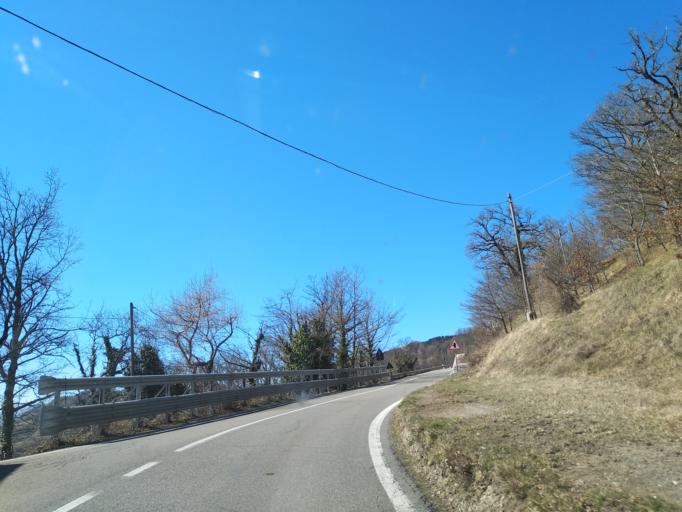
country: IT
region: Emilia-Romagna
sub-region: Provincia di Reggio Emilia
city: Castelnovo ne'Monti
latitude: 44.4187
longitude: 10.3666
